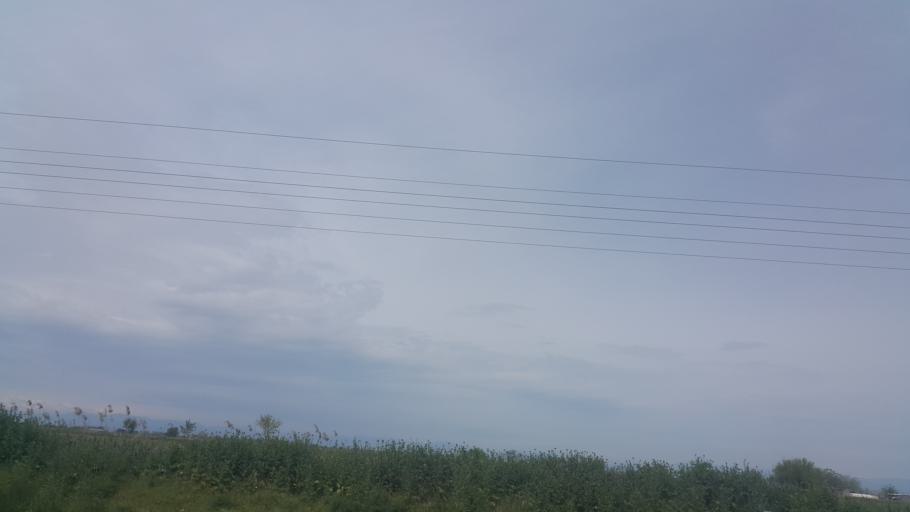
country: TR
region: Adana
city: Ceyhan
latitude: 37.0565
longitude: 35.8786
